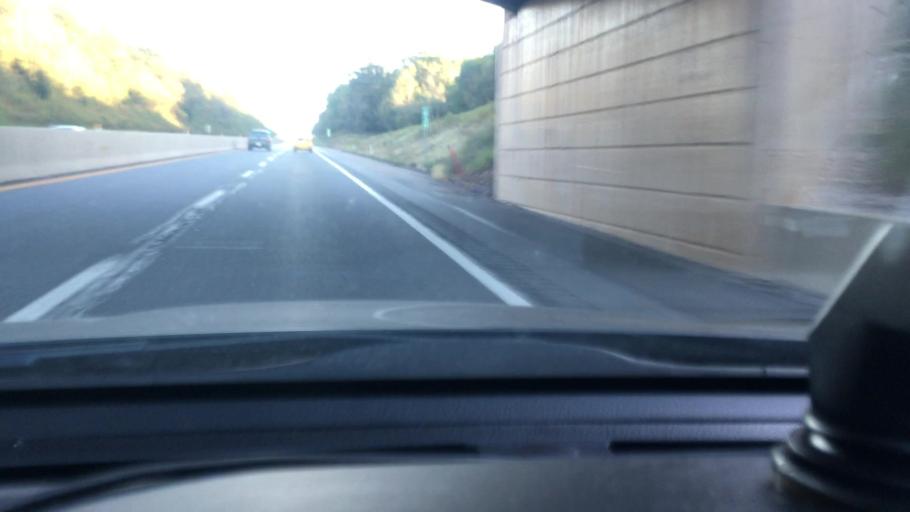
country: US
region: Pennsylvania
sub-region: Carbon County
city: Towamensing Trails
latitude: 40.9386
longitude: -75.6405
